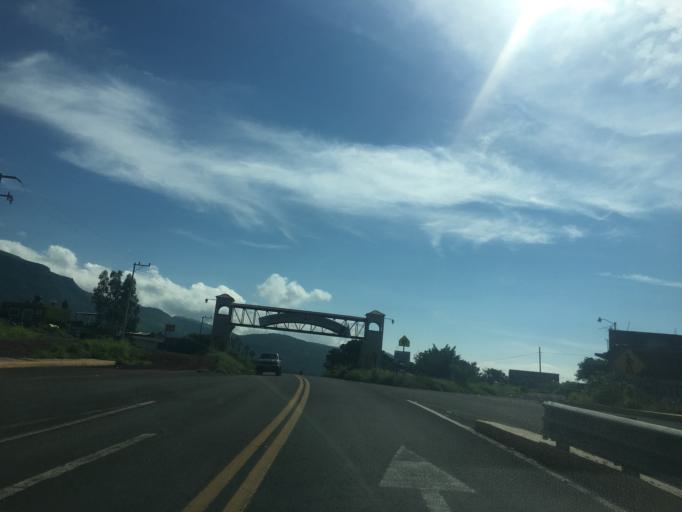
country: MX
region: Nayarit
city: Ixtlan del Rio
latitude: 21.0299
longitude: -104.3543
